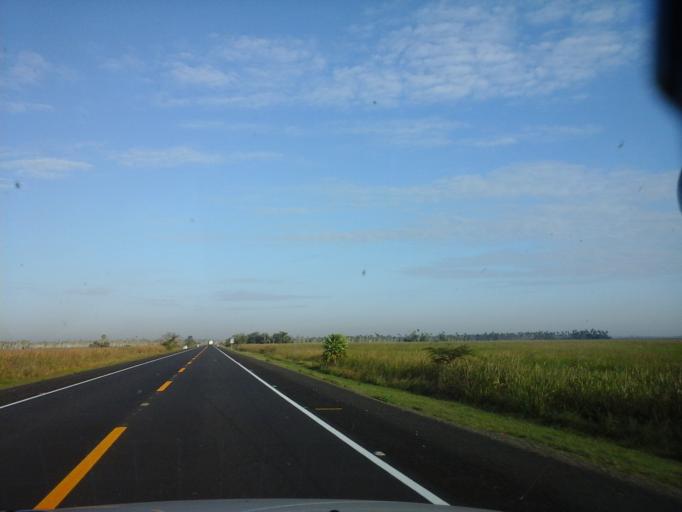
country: PY
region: Neembucu
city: Cerrito
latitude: -26.8931
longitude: -57.7119
